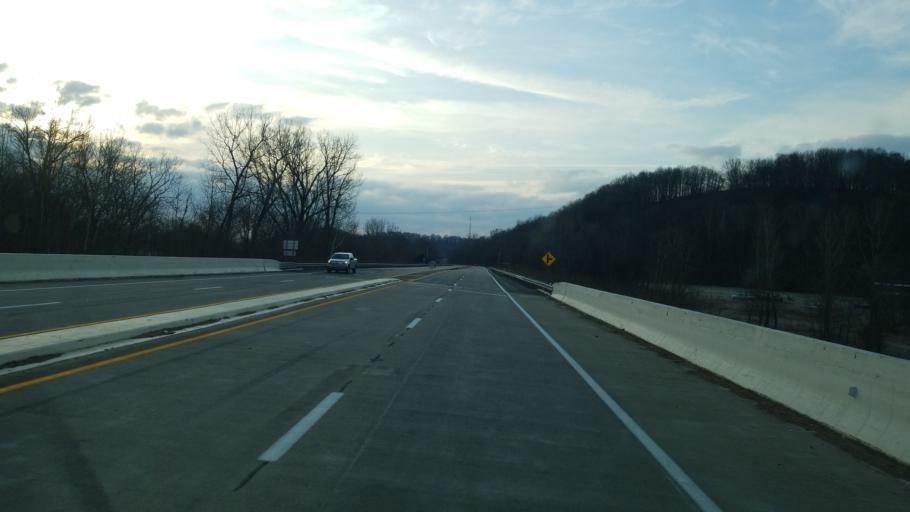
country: US
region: Ohio
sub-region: Ross County
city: Chillicothe
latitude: 39.3071
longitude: -82.9600
